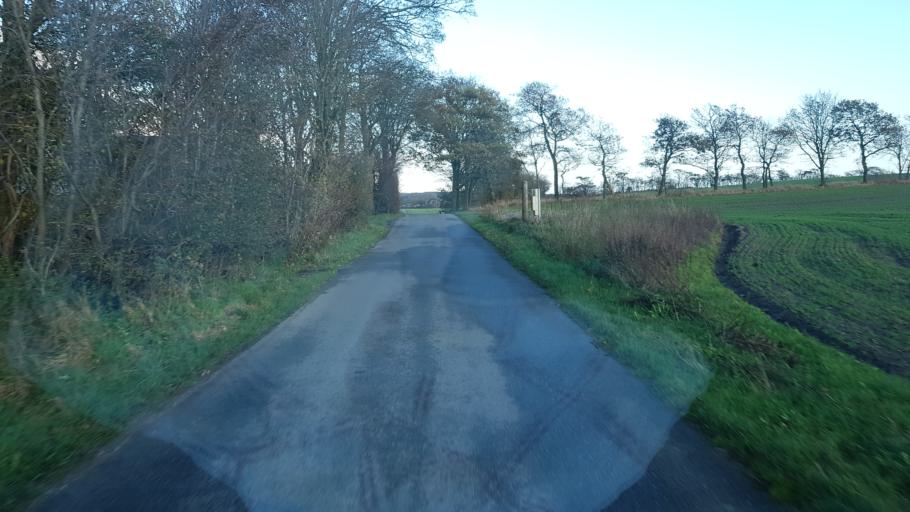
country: DK
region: South Denmark
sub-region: Vejen Kommune
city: Brorup
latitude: 55.4566
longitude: 8.9764
